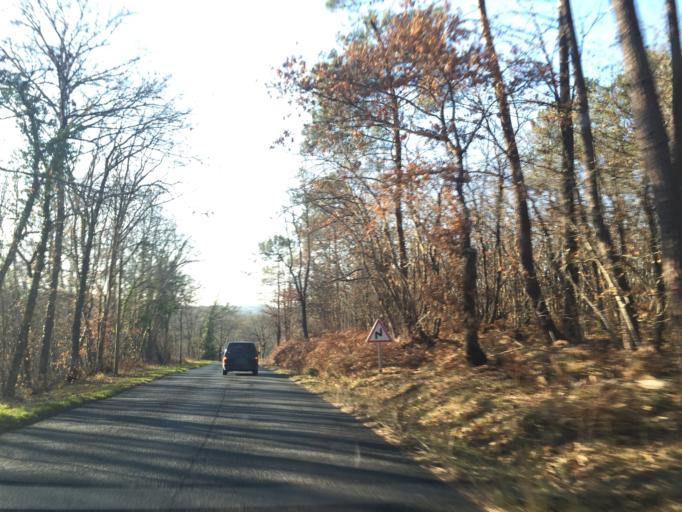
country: FR
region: Aquitaine
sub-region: Departement de la Dordogne
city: Neuvic
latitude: 45.1368
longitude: 0.4669
